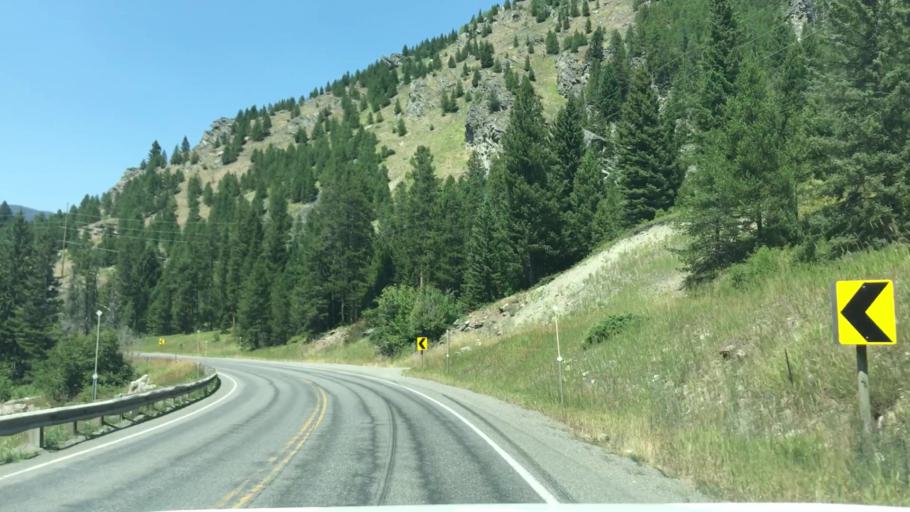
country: US
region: Montana
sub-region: Gallatin County
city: Big Sky
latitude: 45.3896
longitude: -111.1982
